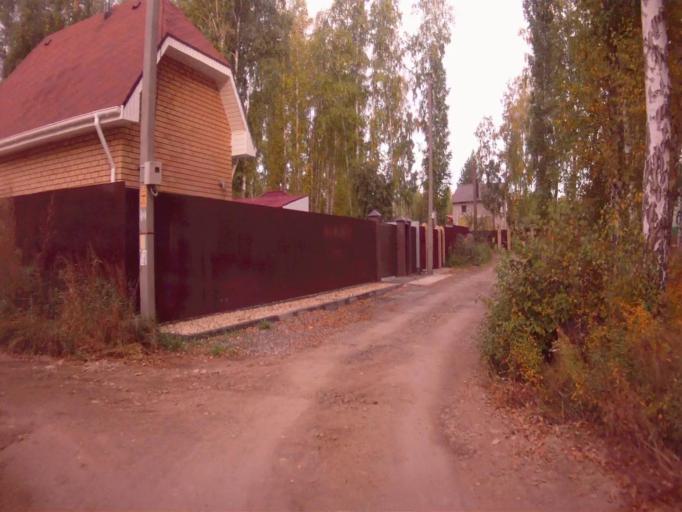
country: RU
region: Chelyabinsk
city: Sargazy
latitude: 55.1286
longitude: 61.2495
